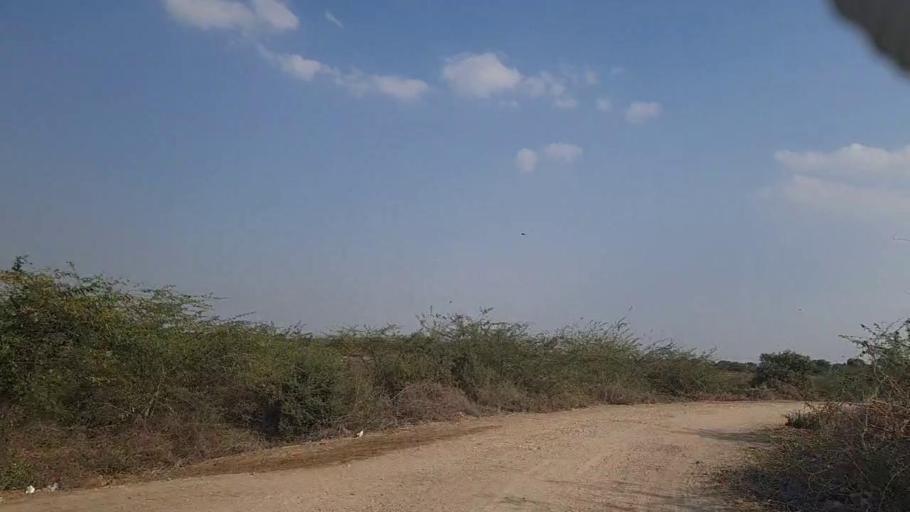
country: PK
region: Sindh
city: Jati
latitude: 24.4294
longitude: 68.3758
